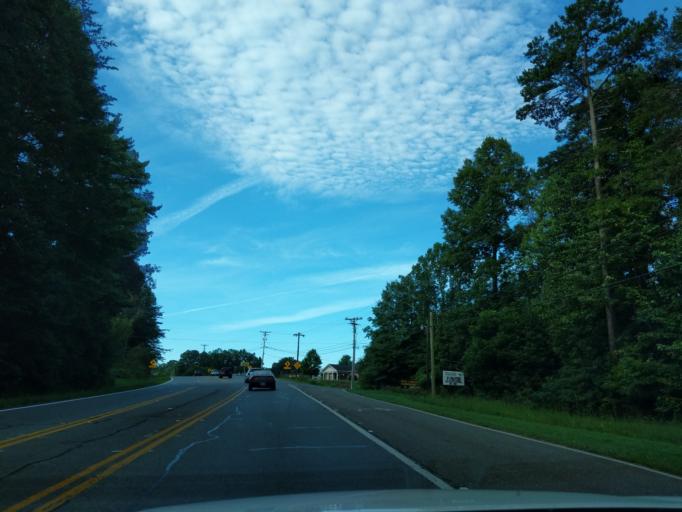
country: US
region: Georgia
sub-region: Fannin County
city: McCaysville
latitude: 34.9231
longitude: -84.3777
